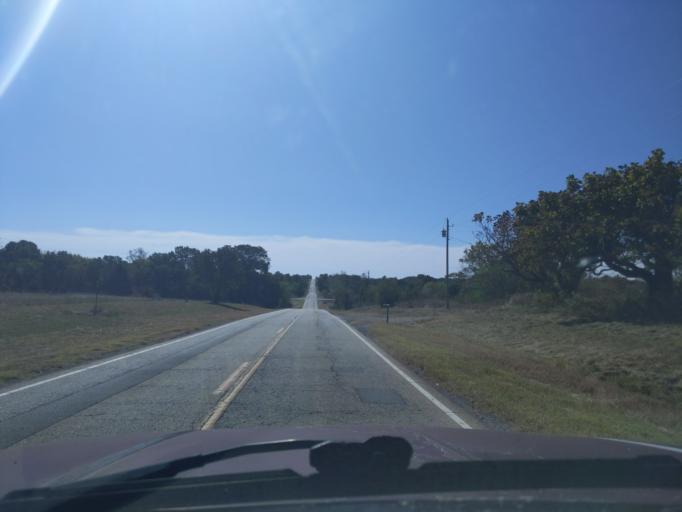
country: US
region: Oklahoma
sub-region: Creek County
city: Bristow
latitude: 35.7149
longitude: -96.3873
